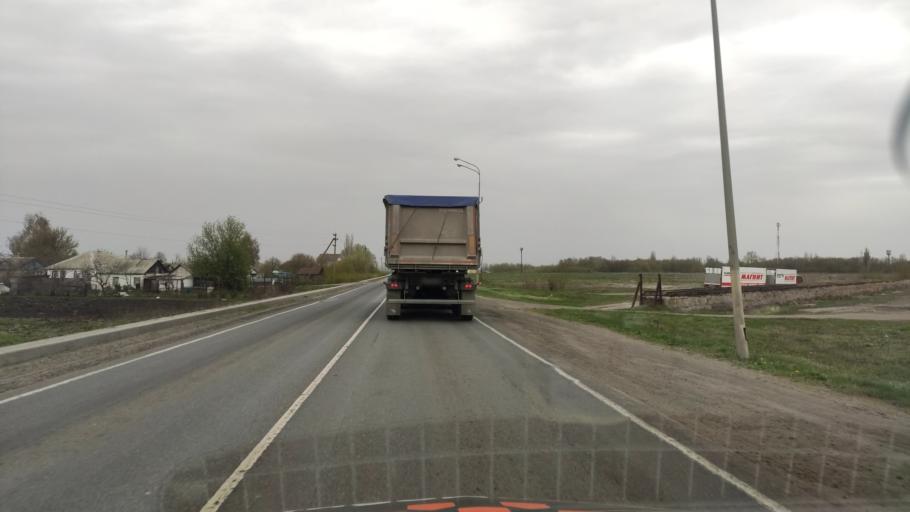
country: RU
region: Kursk
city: Gorshechnoye
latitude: 51.5280
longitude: 38.0228
